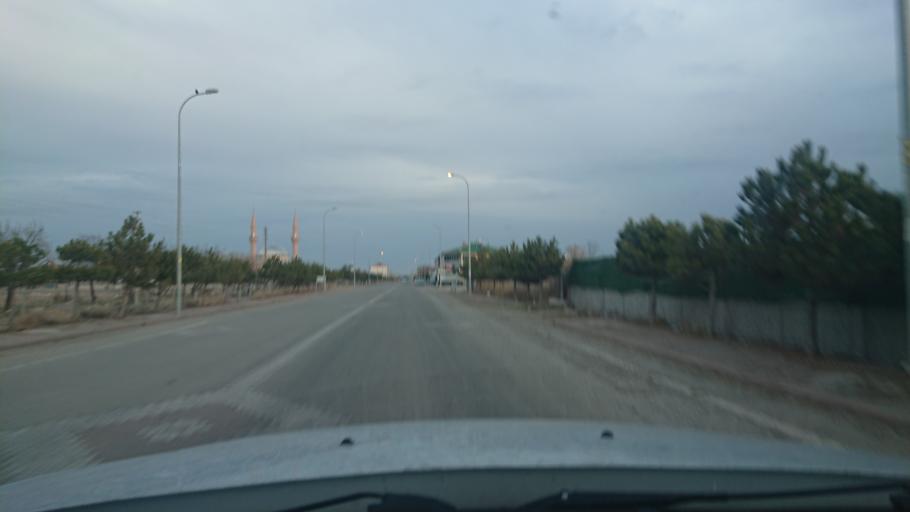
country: TR
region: Aksaray
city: Yesilova
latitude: 38.3314
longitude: 33.7521
